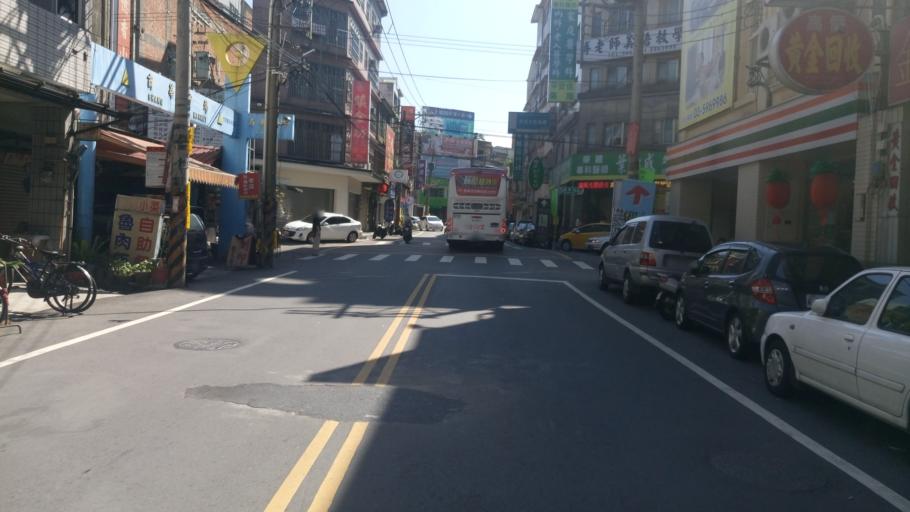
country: TW
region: Taiwan
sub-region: Hsinchu
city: Zhubei
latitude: 24.7375
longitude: 121.0878
